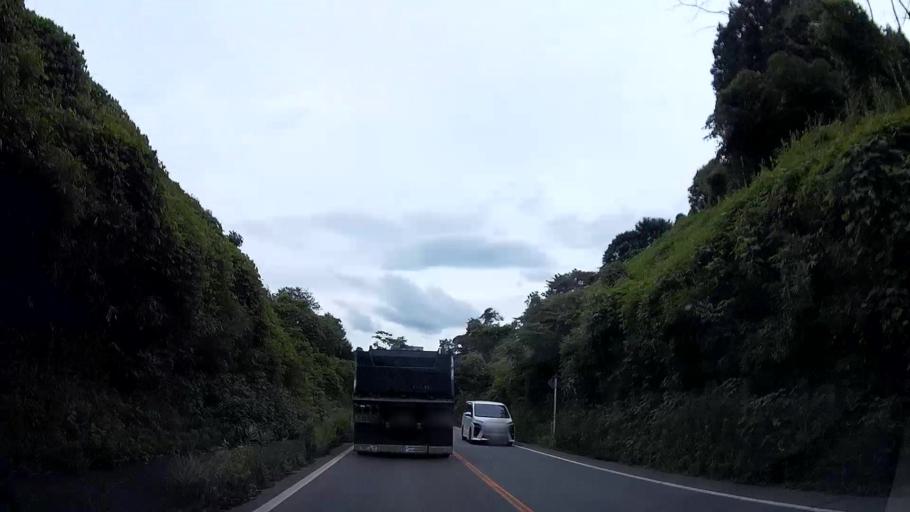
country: JP
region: Oita
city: Tsukawaki
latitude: 33.1259
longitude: 131.0609
